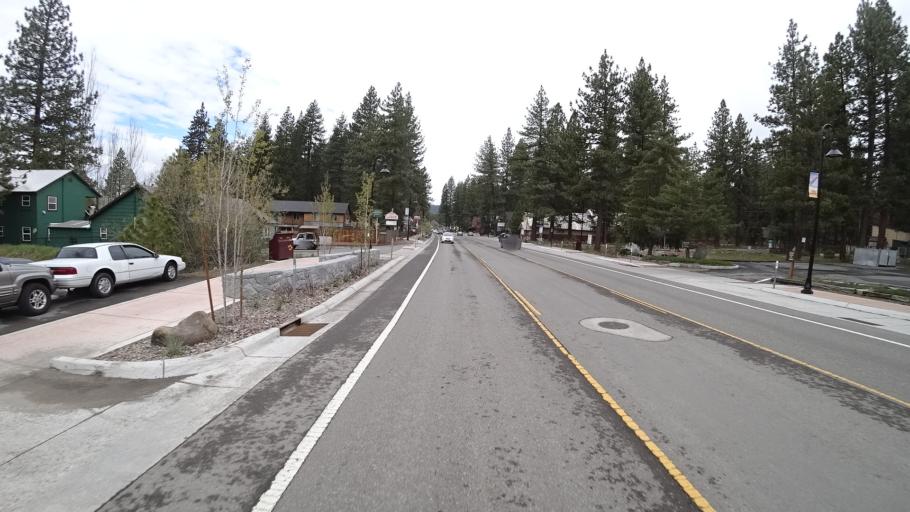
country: US
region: California
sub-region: Placer County
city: Kings Beach
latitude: 39.2343
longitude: -120.0173
